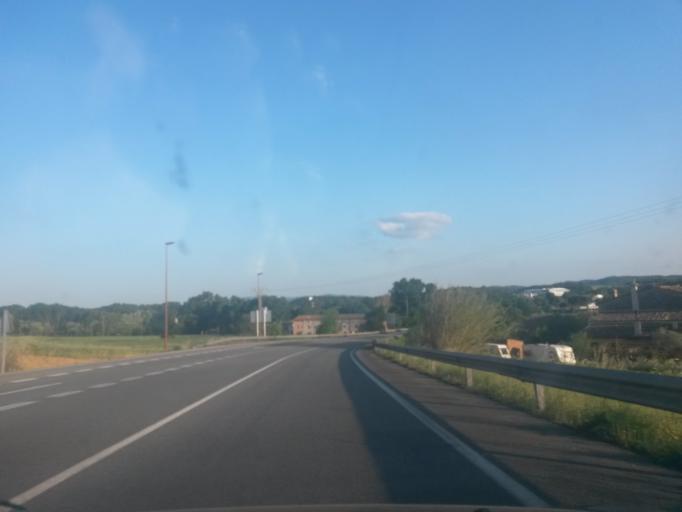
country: ES
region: Catalonia
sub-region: Provincia de Girona
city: Cornella del Terri
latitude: 42.1034
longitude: 2.7964
